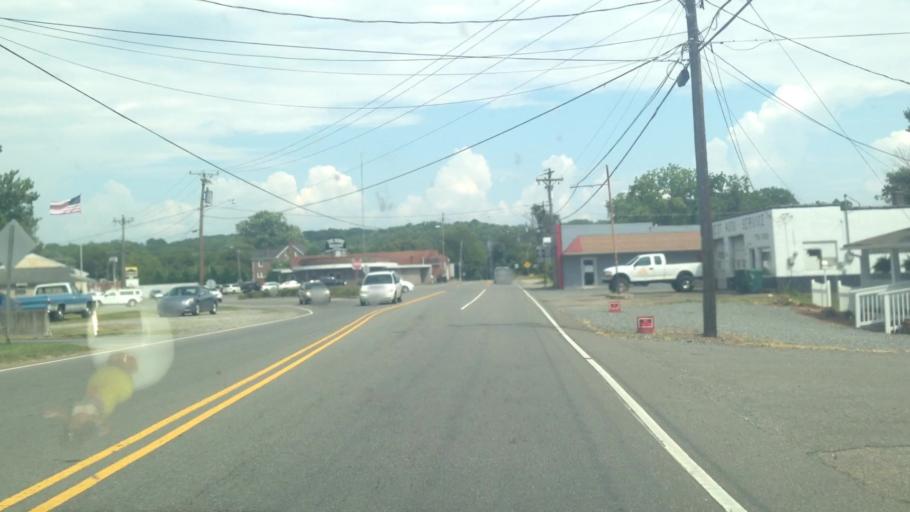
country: US
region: North Carolina
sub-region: Surry County
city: Mount Airy
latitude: 36.4860
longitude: -80.5902
